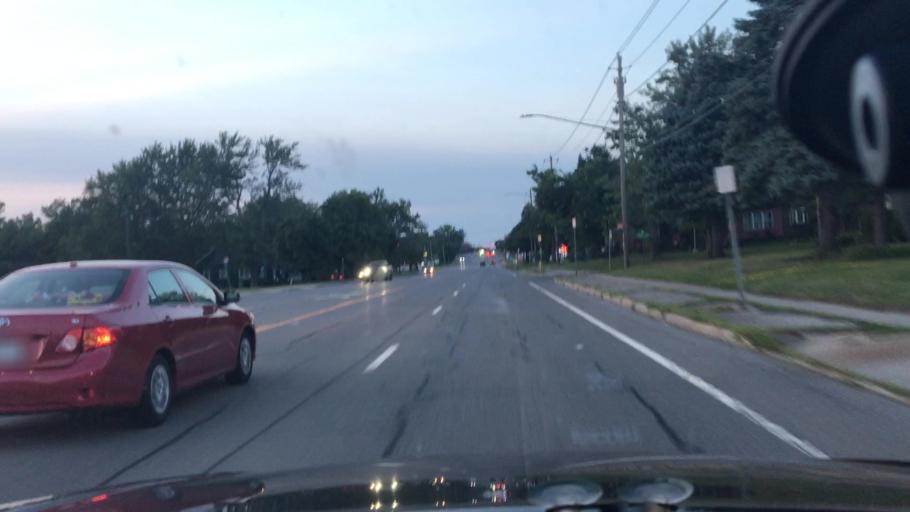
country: US
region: New York
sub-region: Erie County
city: Cheektowaga
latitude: 42.8607
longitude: -78.7544
